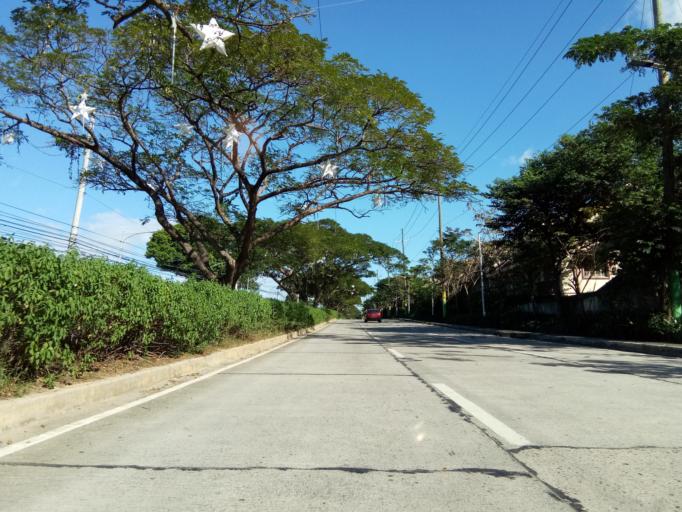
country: PH
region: Calabarzon
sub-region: Province of Cavite
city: Dasmarinas
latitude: 14.3511
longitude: 120.9580
